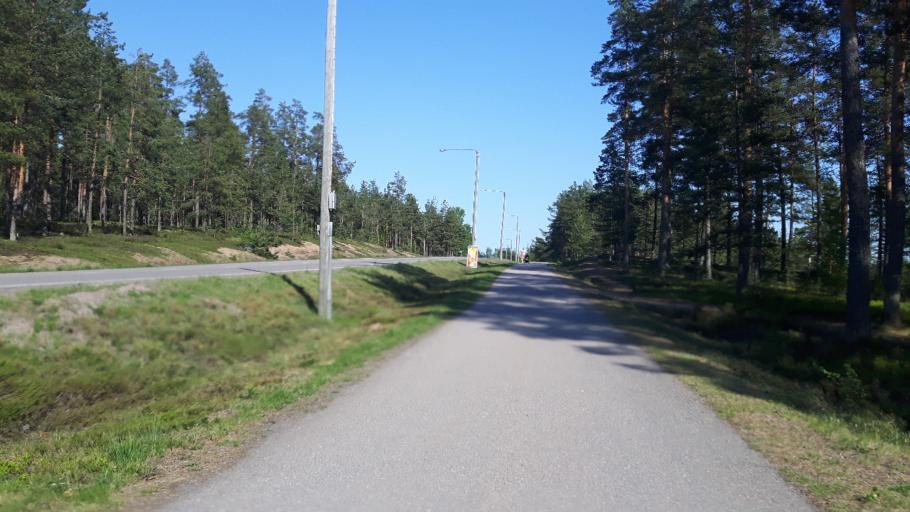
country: FI
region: Kymenlaakso
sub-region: Kotka-Hamina
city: Broby
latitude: 60.4875
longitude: 26.7500
